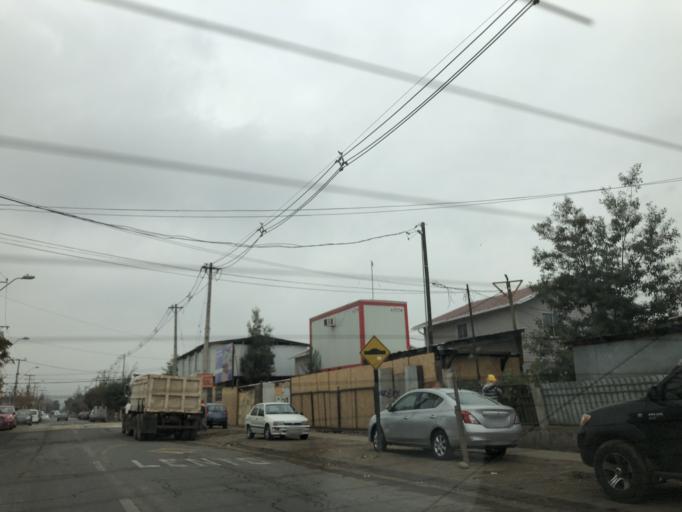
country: CL
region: Santiago Metropolitan
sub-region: Provincia de Santiago
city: La Pintana
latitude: -33.5847
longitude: -70.6052
